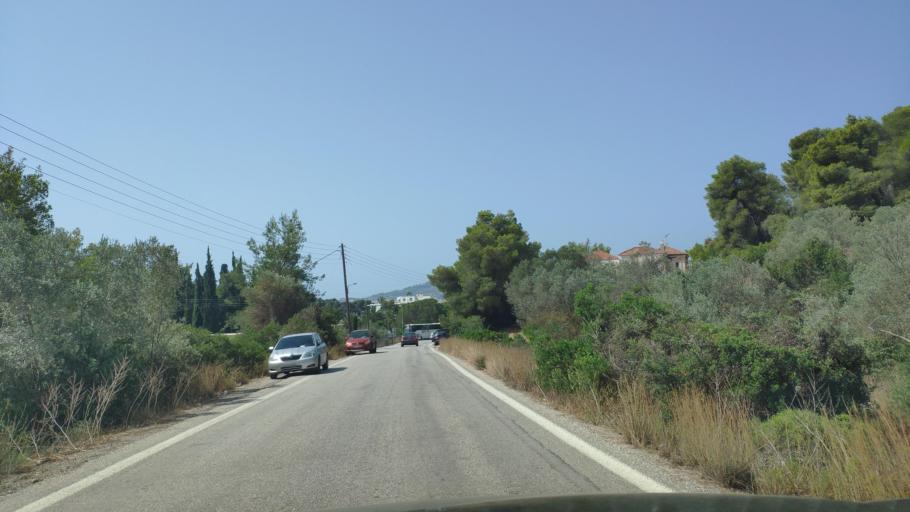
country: GR
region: Peloponnese
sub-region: Nomos Argolidos
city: Porto Cheli
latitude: 37.2985
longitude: 23.1645
